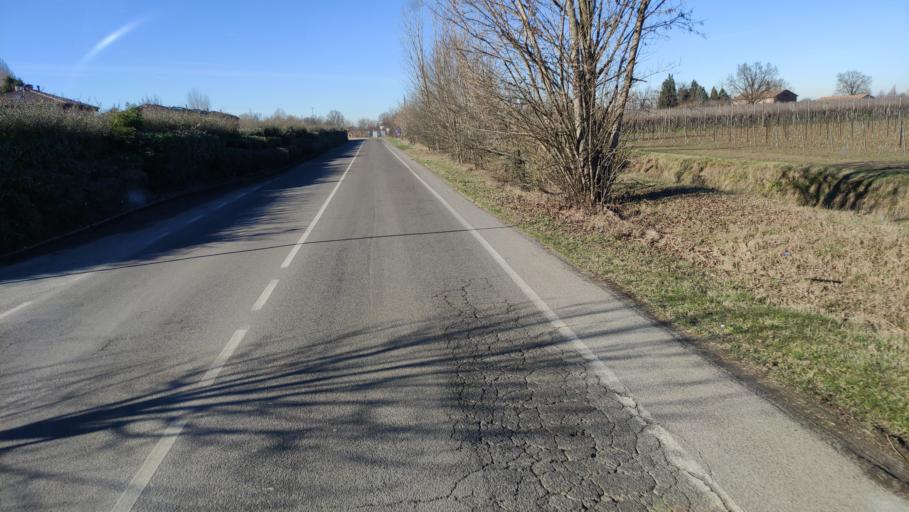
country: IT
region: Emilia-Romagna
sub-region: Provincia di Reggio Emilia
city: Correggio
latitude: 44.7800
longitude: 10.7878
